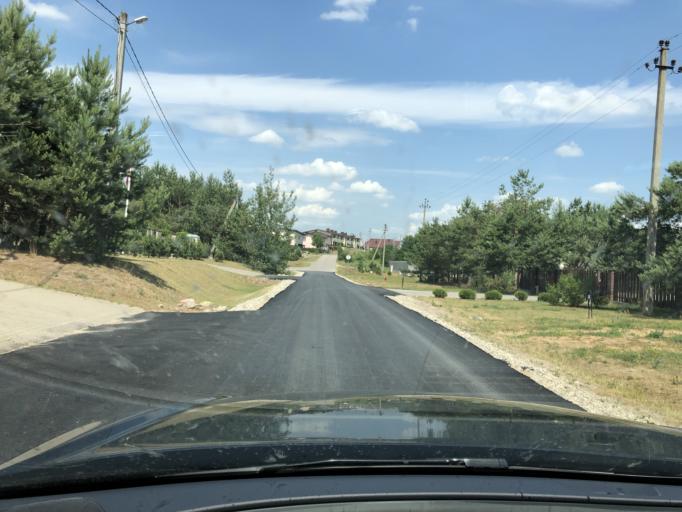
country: LT
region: Vilnius County
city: Pasilaiciai
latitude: 54.7496
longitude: 25.1909
